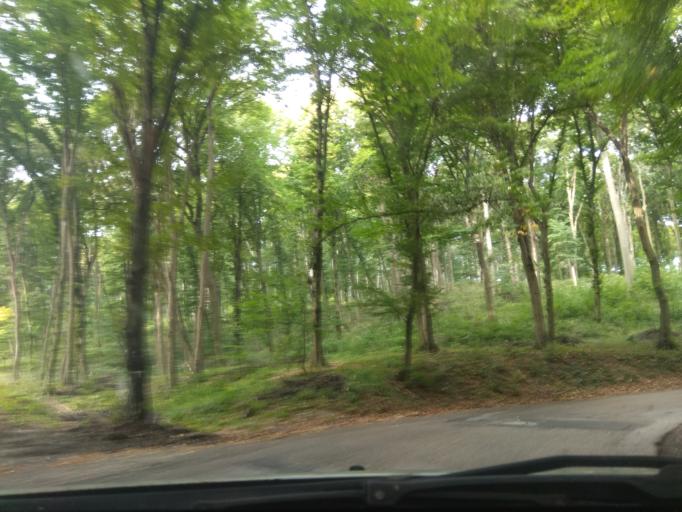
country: HU
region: Borsod-Abauj-Zemplen
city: Miskolc
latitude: 48.0636
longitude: 20.6815
